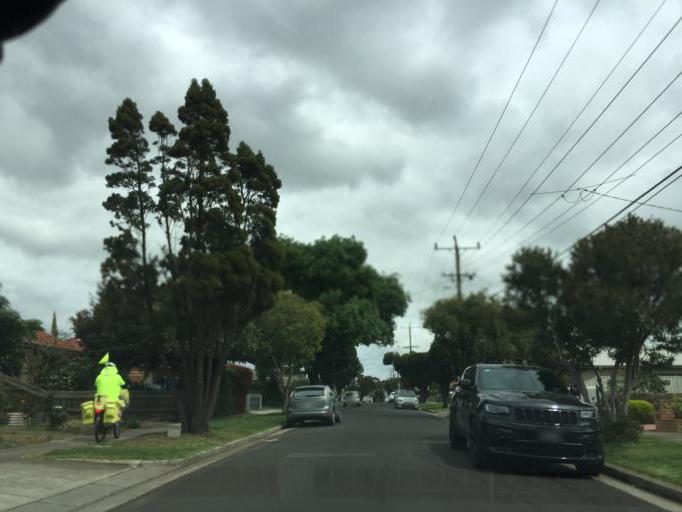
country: AU
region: Victoria
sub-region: Brimbank
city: Brooklyn
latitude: -37.8209
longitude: 144.8461
